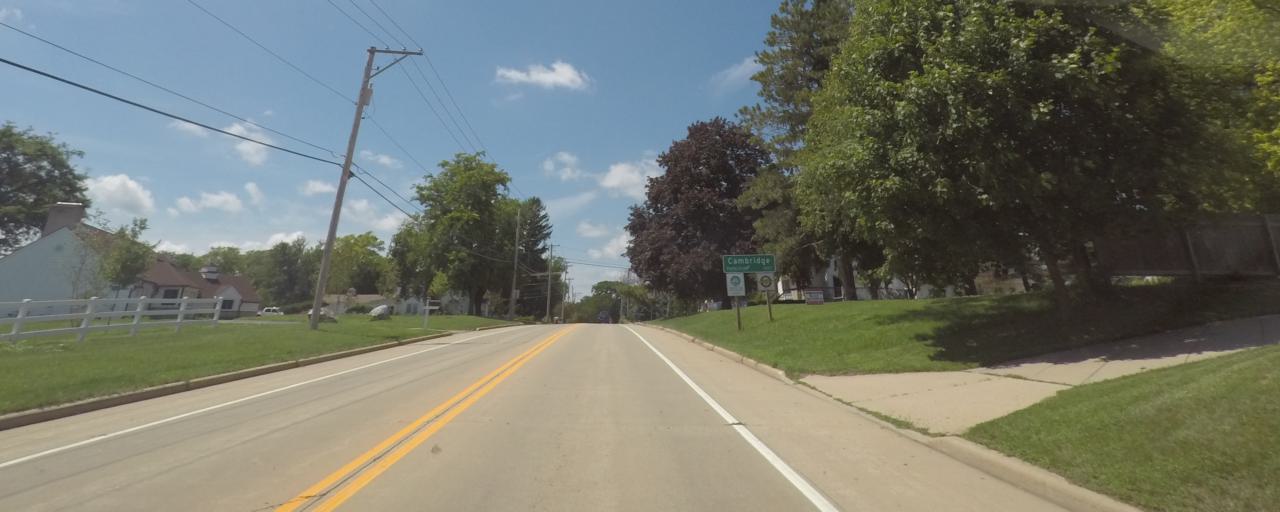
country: US
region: Wisconsin
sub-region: Jefferson County
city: Cambridge
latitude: 43.0020
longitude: -89.0103
